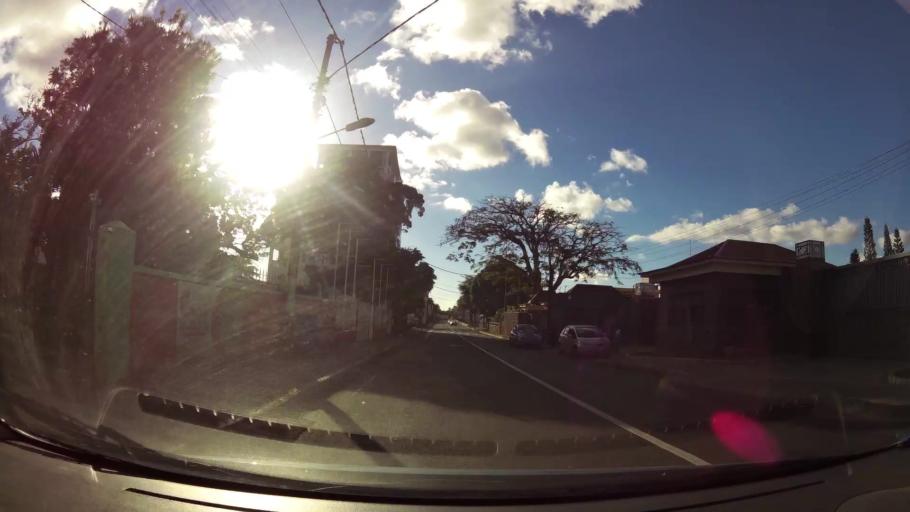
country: MU
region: Plaines Wilhems
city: Ebene
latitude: -20.2516
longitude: 57.4846
